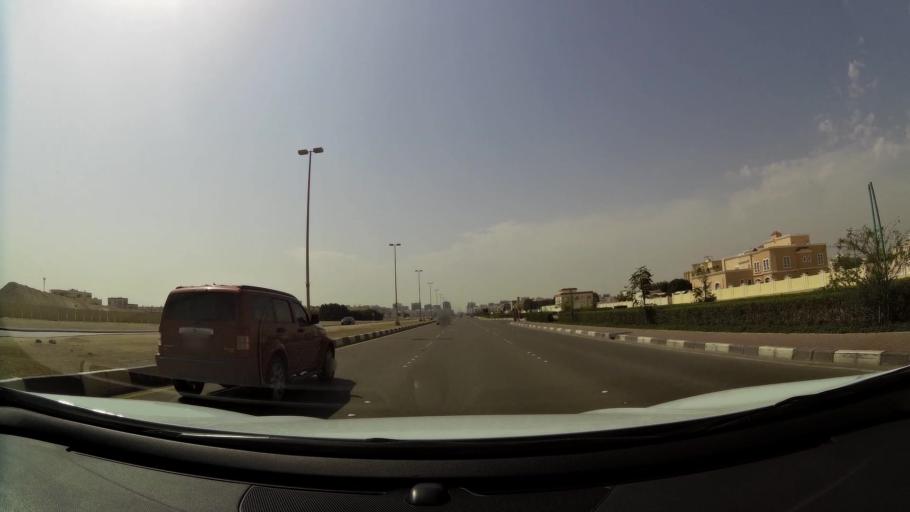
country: AE
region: Abu Dhabi
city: Abu Dhabi
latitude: 24.3252
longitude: 54.5496
